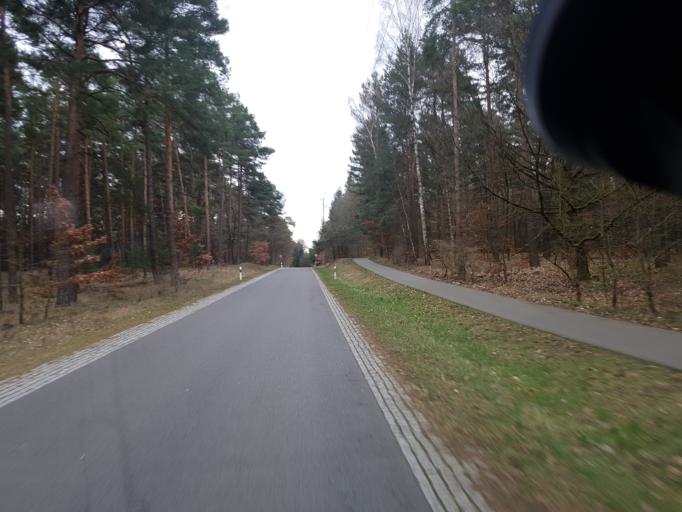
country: DE
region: Brandenburg
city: Mixdorf
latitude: 52.1881
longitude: 14.4281
